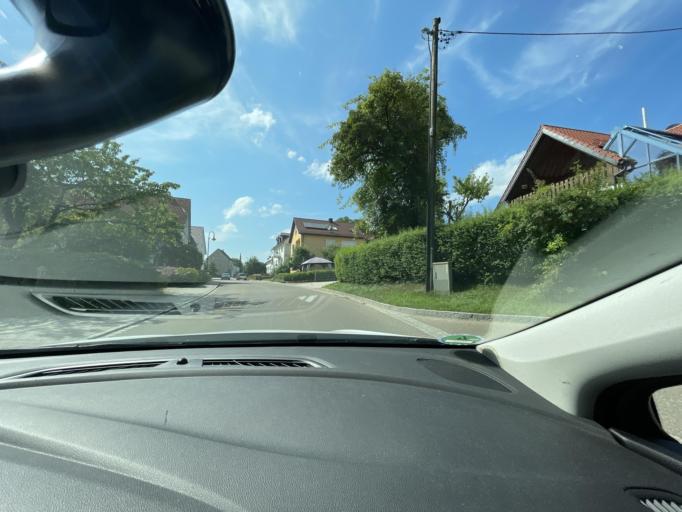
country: DE
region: Bavaria
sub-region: Upper Bavaria
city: Hilgertshausen-Tandern
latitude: 48.4240
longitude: 11.3097
